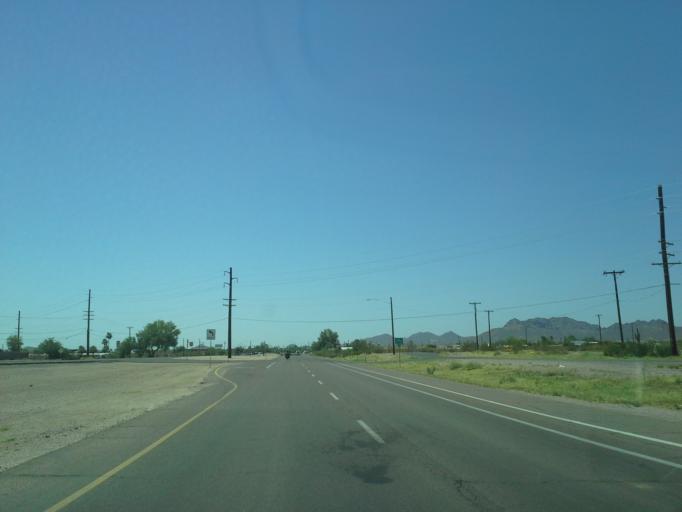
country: US
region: Arizona
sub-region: Pinal County
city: Apache Junction
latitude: 33.4073
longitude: -111.5361
